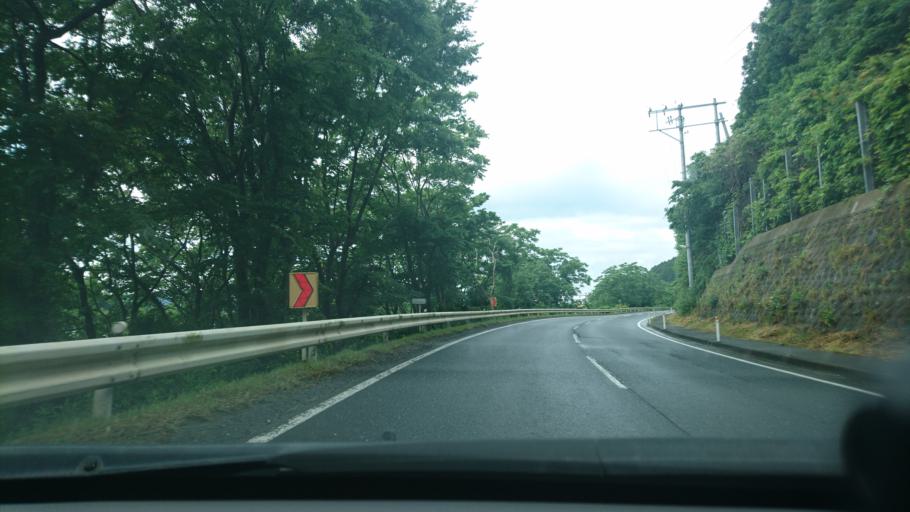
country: JP
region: Miyagi
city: Wakuya
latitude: 38.5958
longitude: 141.3041
